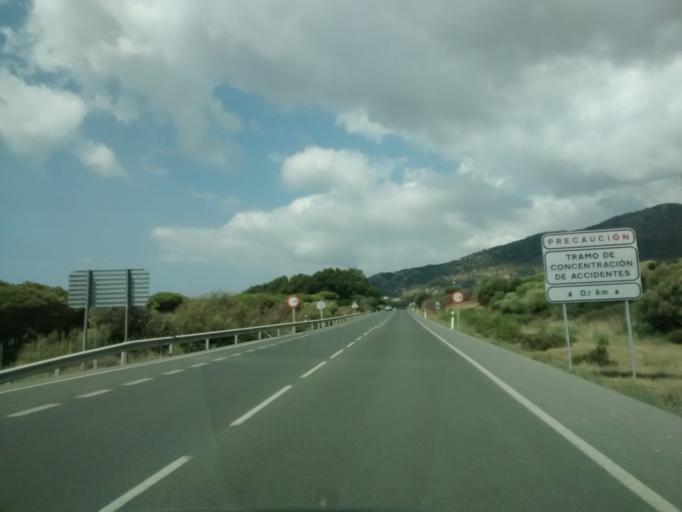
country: ES
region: Andalusia
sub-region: Provincia de Cadiz
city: Tarifa
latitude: 36.0494
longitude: -5.6410
